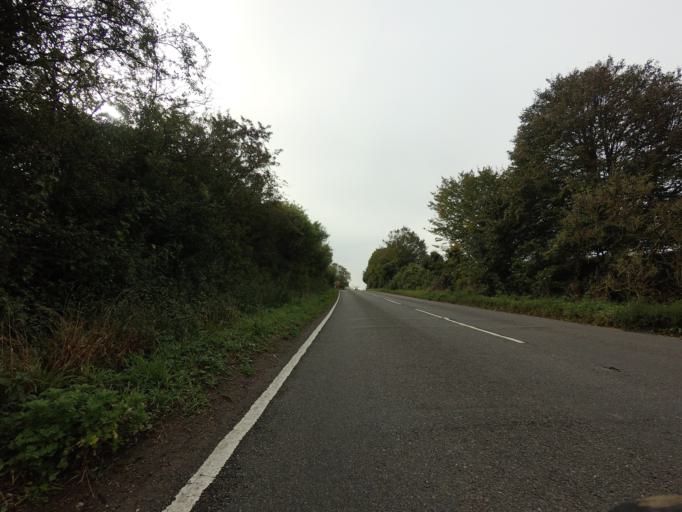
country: GB
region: England
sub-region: Cambridgeshire
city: Melbourn
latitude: 52.0341
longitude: 0.0410
